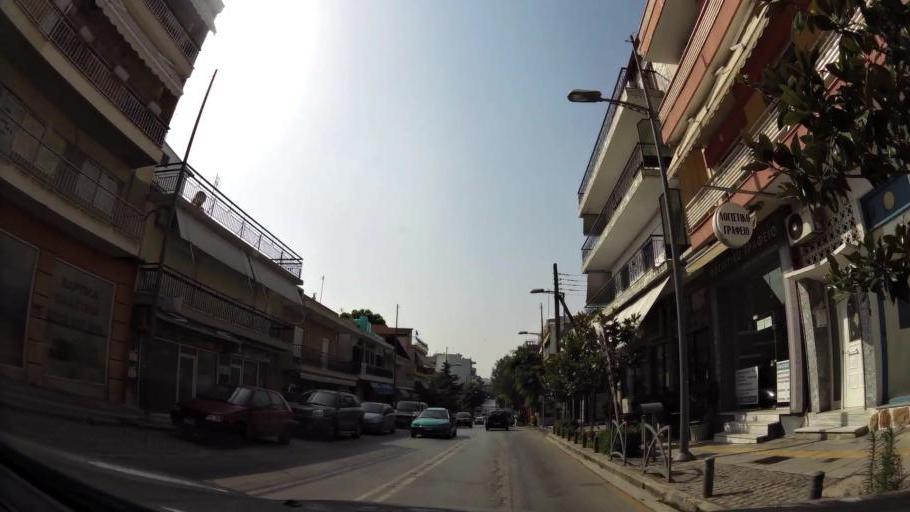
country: GR
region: Central Macedonia
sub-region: Nomos Thessalonikis
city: Stavroupoli
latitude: 40.6709
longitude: 22.9311
